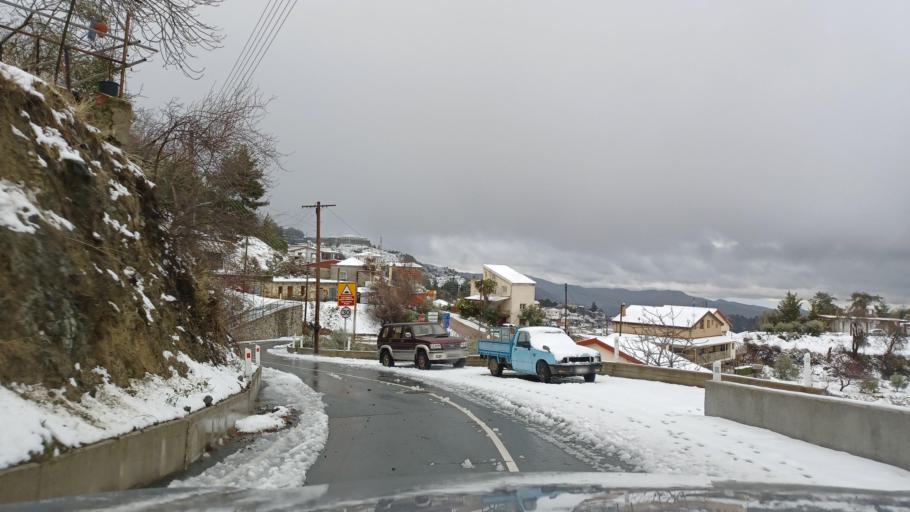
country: CY
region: Limassol
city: Pelendri
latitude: 34.9009
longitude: 32.9646
